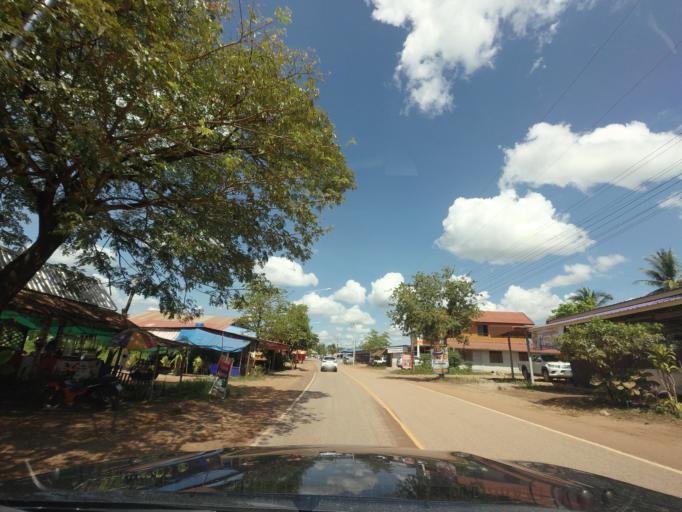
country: TH
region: Changwat Udon Thani
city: Ban Dung
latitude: 17.7411
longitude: 103.3577
